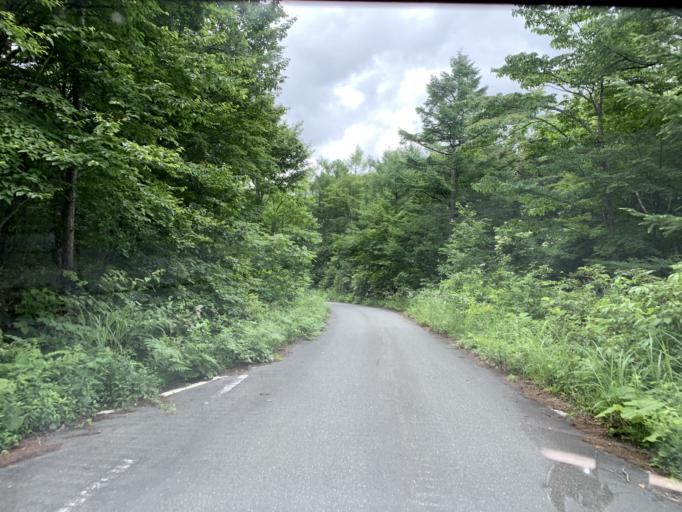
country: JP
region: Iwate
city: Ichinoseki
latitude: 38.9406
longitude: 140.8762
